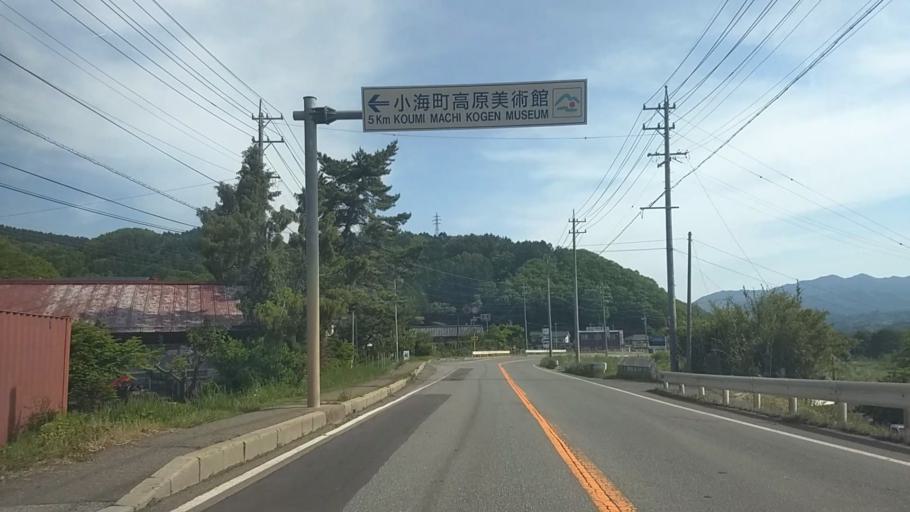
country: JP
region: Nagano
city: Saku
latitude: 36.0575
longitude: 138.4672
